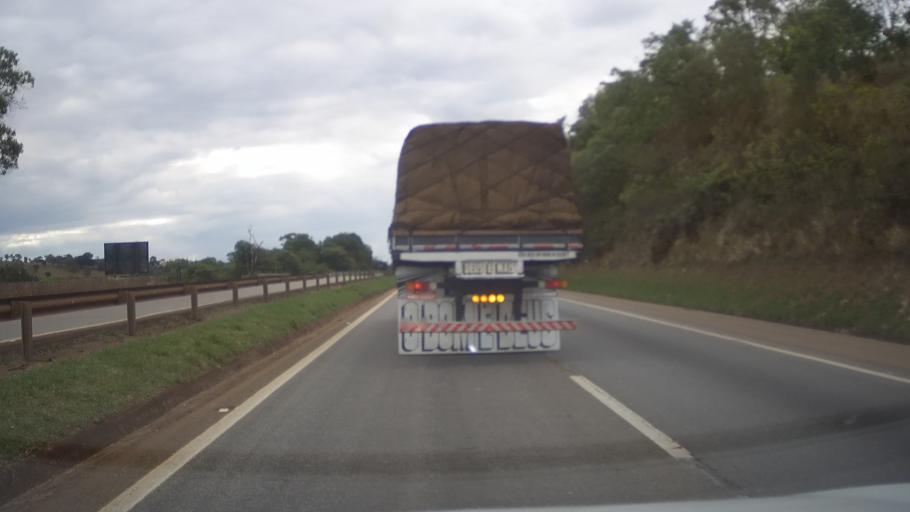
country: BR
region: Minas Gerais
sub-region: Itauna
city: Itauna
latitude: -20.3302
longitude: -44.4526
